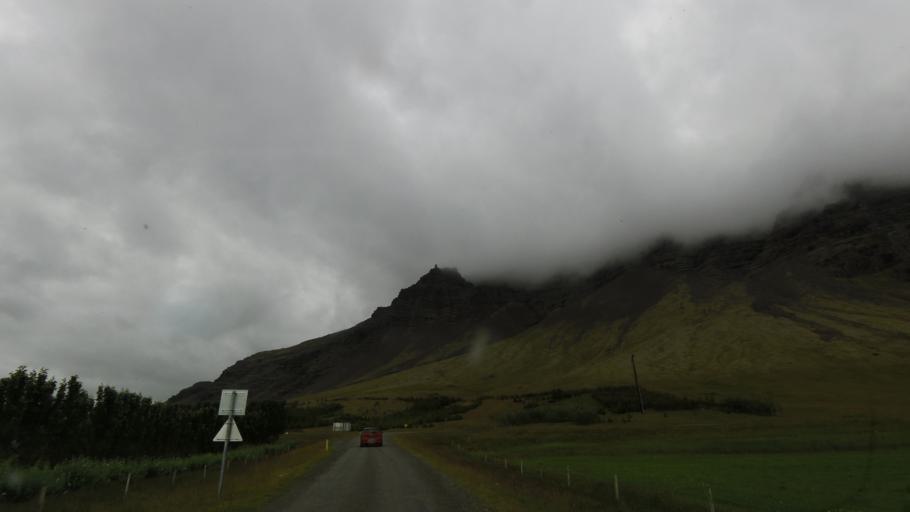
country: IS
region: East
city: Hoefn
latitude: 64.1302
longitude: -16.0173
